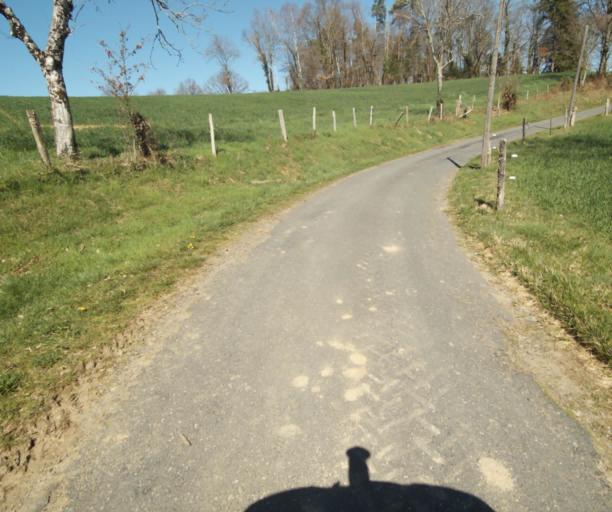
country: FR
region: Limousin
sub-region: Departement de la Correze
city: Saint-Mexant
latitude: 45.3017
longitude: 1.6463
